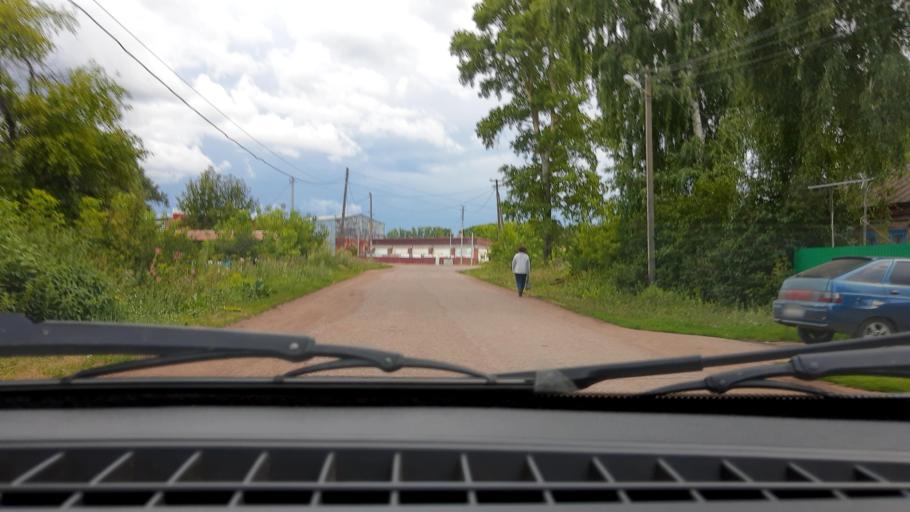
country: RU
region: Bashkortostan
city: Mikhaylovka
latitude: 54.8625
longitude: 55.8154
